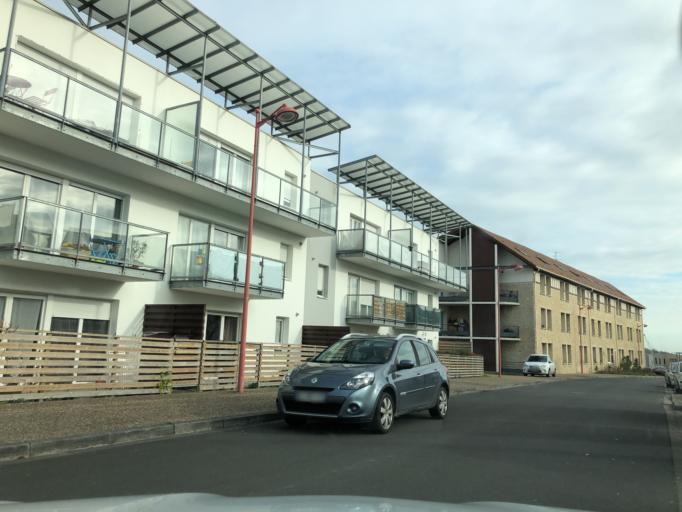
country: FR
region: Lower Normandy
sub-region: Departement du Calvados
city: Blainville-sur-Orne
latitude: 49.2315
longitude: -0.3013
